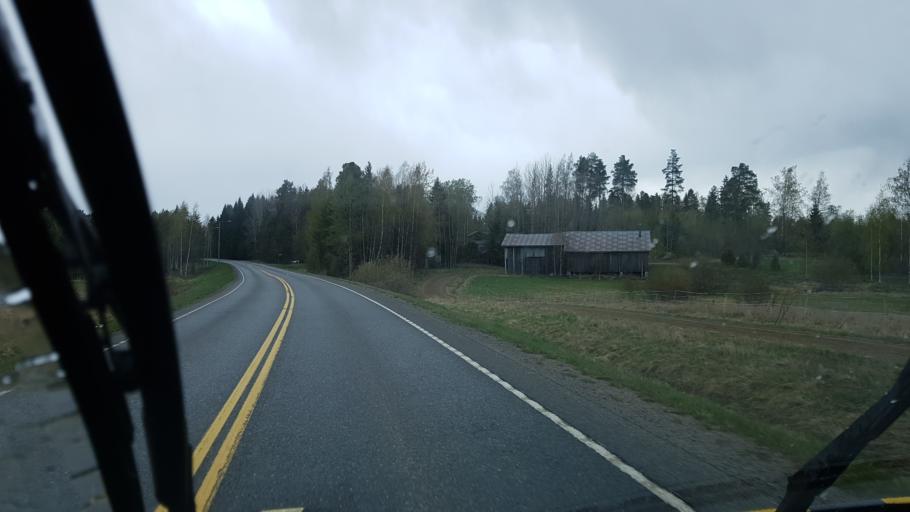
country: FI
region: Pirkanmaa
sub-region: Tampere
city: Pirkkala
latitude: 61.4260
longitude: 23.6336
